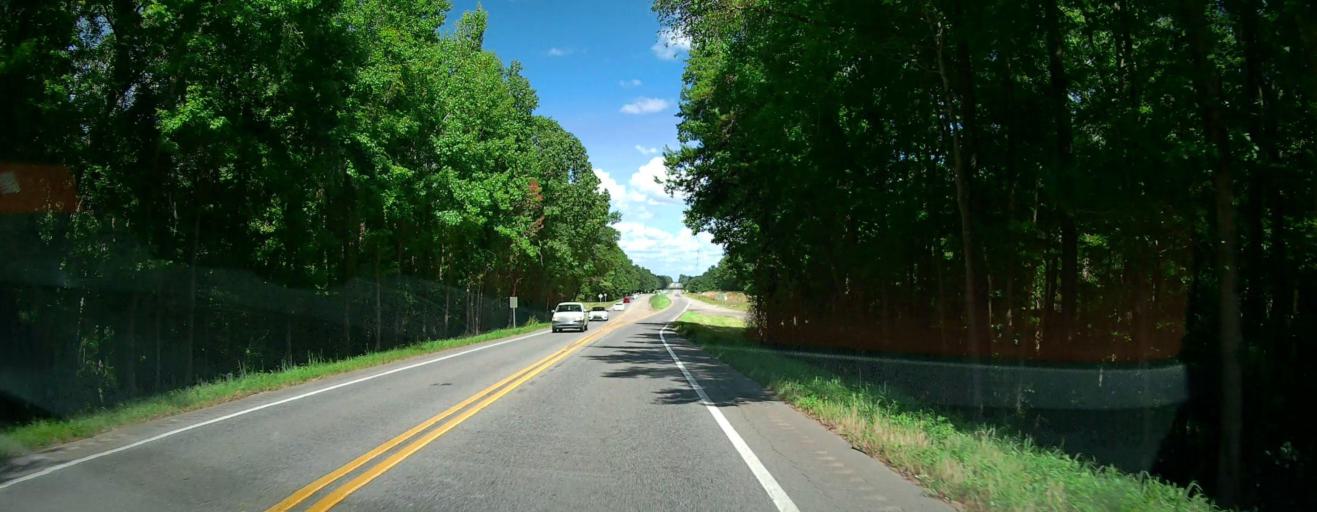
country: US
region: Alabama
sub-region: Pickens County
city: Gordo
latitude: 33.2844
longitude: -87.8407
